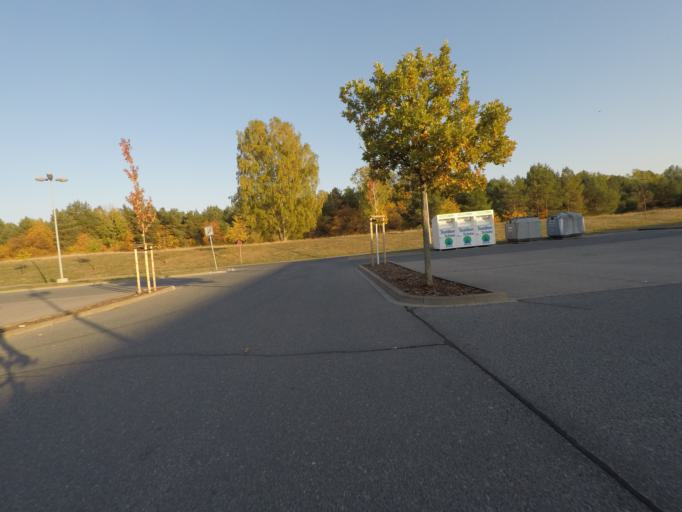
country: DE
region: Brandenburg
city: Melchow
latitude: 52.8387
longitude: 13.7017
